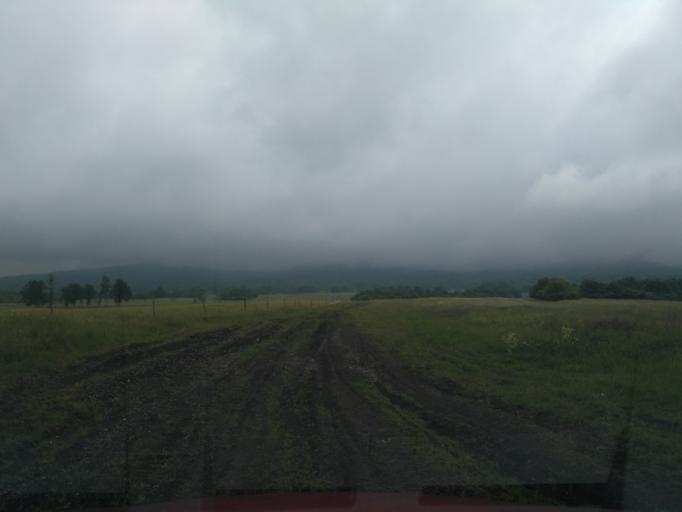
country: SK
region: Kosicky
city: Secovce
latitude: 48.7662
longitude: 21.4959
